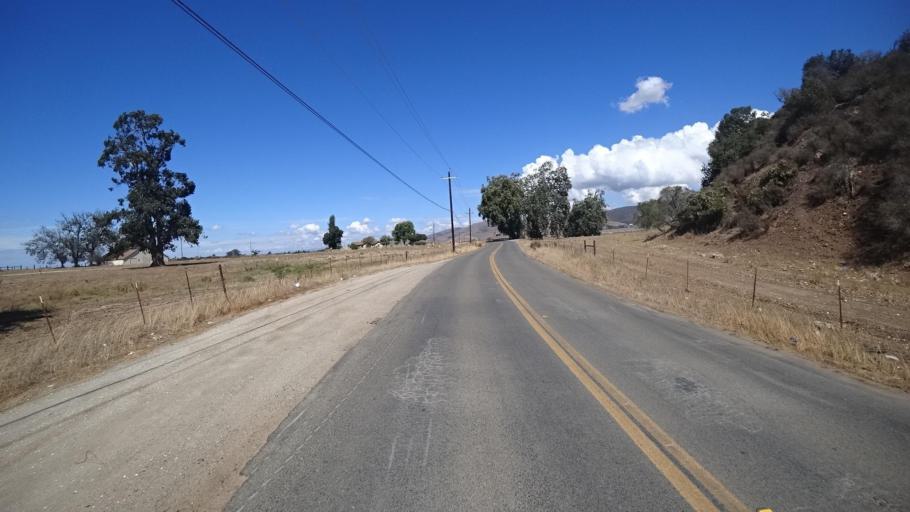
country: US
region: California
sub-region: Monterey County
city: Salinas
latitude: 36.6911
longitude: -121.5691
